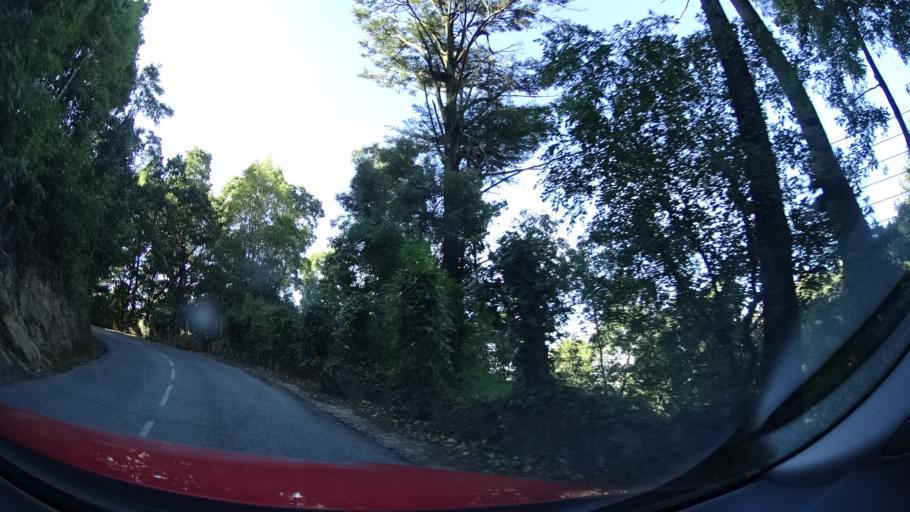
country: PT
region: Lisbon
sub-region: Sintra
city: Sintra
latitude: 38.7928
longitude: -9.3967
